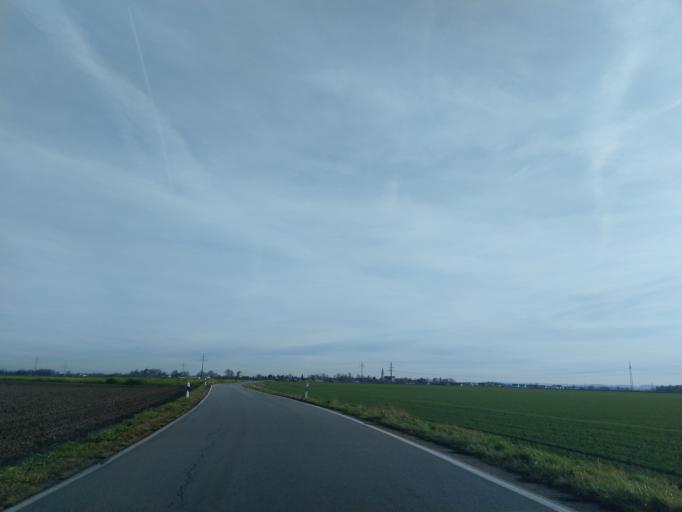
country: DE
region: Bavaria
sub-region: Lower Bavaria
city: Otzing
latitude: 48.7664
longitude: 12.7893
